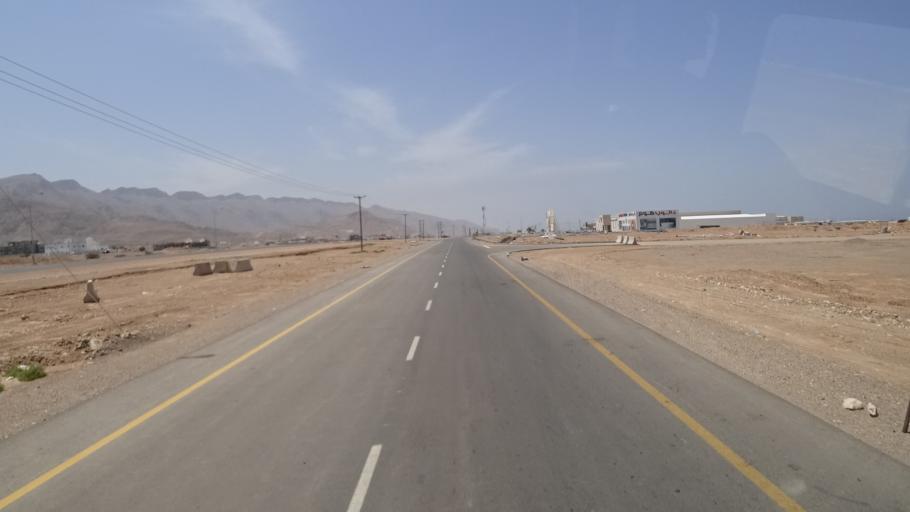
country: OM
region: Ash Sharqiyah
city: Sur
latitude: 22.5912
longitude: 59.4395
